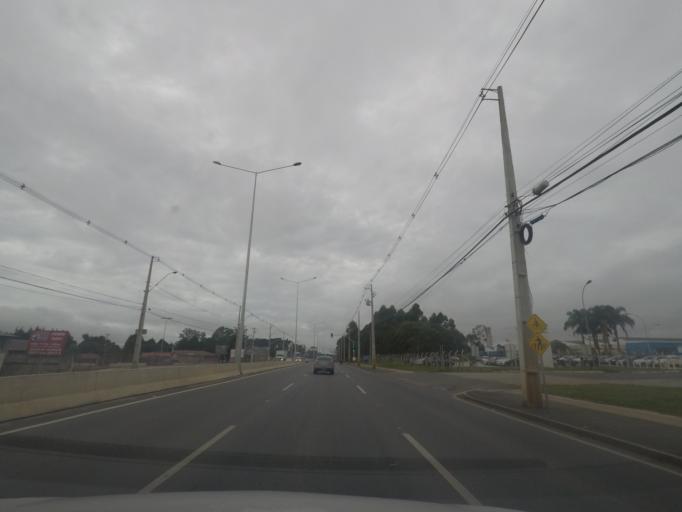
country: BR
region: Parana
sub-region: Piraquara
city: Piraquara
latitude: -25.4583
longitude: -49.1004
